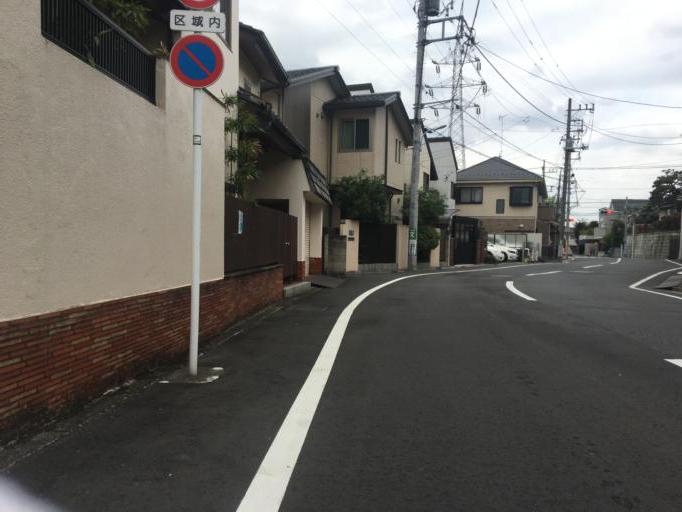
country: JP
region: Tokyo
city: Tokyo
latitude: 35.6725
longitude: 139.6376
